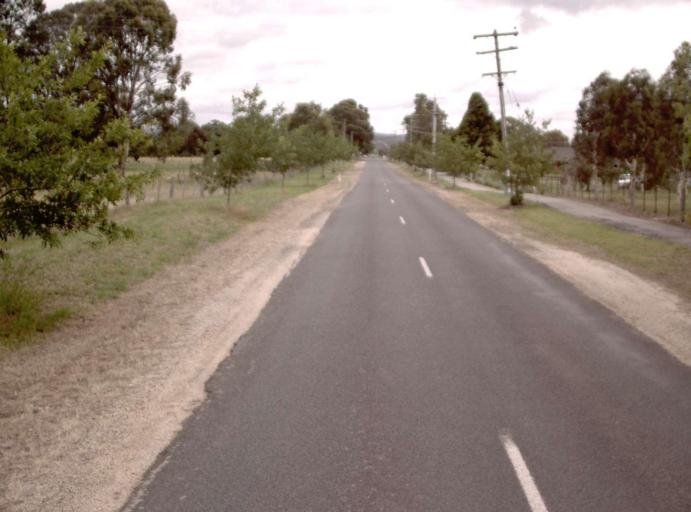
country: AU
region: Victoria
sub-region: Wellington
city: Sale
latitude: -37.8478
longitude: 147.0718
